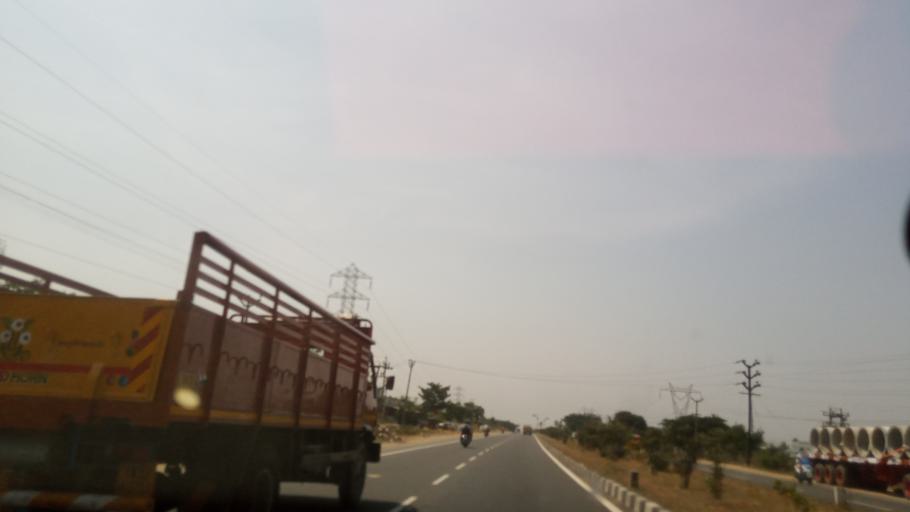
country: IN
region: Tamil Nadu
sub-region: Salem
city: Salem
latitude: 11.6533
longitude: 78.1958
